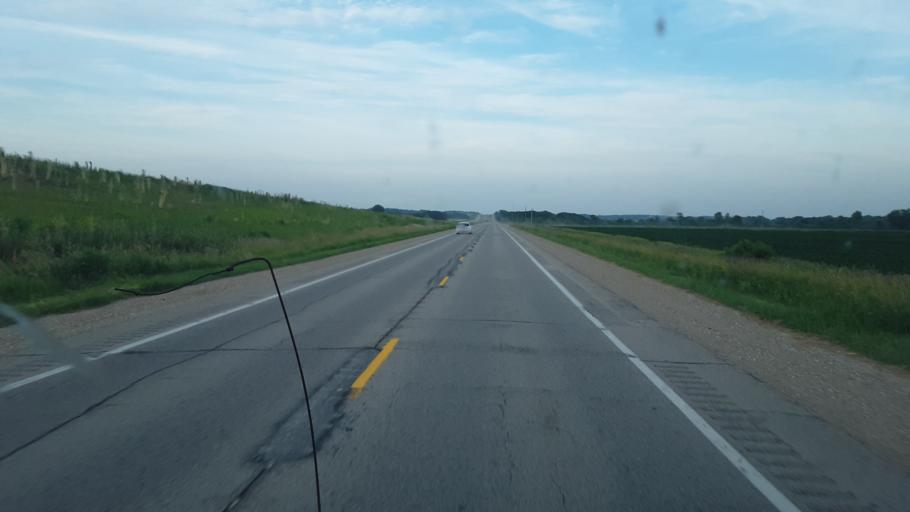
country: US
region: Iowa
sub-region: Tama County
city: Tama
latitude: 41.9638
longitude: -92.4924
